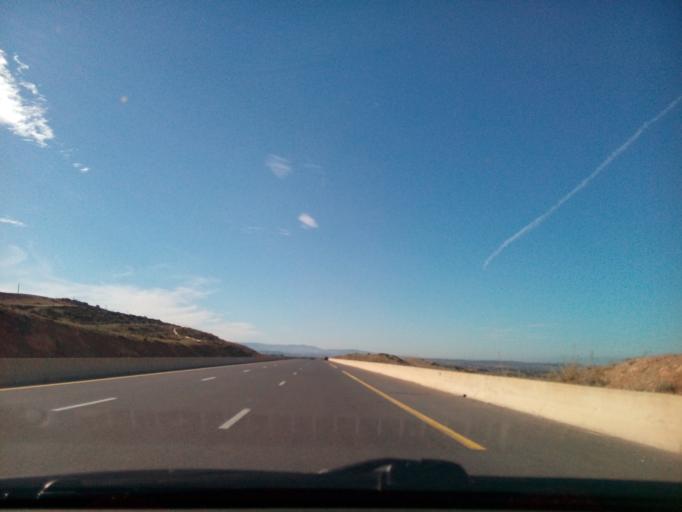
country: DZ
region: Tlemcen
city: Sidi Abdelli
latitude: 35.0146
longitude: -1.1538
